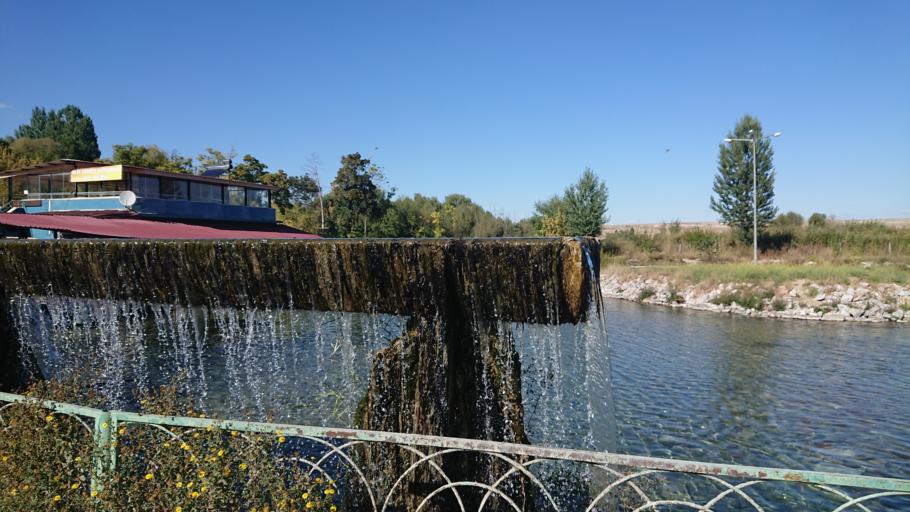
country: TR
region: Eskisehir
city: Cifteler
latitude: 39.3527
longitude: 31.0588
